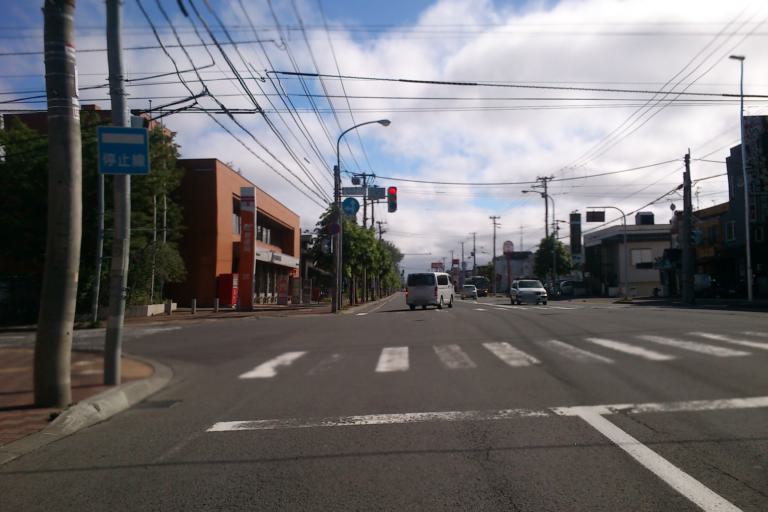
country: JP
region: Hokkaido
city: Sapporo
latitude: 43.1266
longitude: 141.2551
